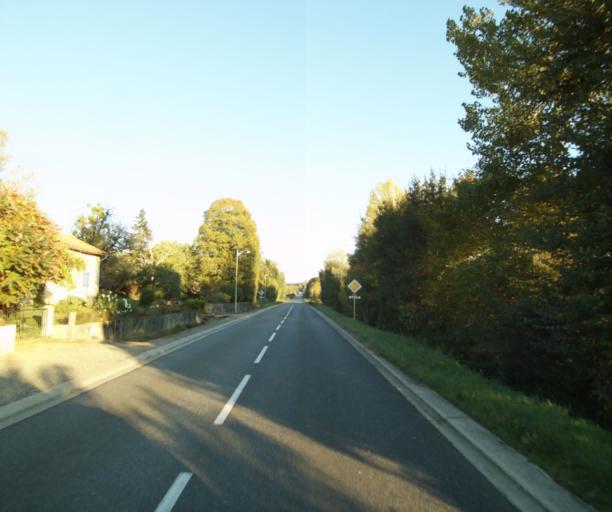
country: FR
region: Midi-Pyrenees
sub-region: Departement du Gers
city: Eauze
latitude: 43.7641
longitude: 0.1712
